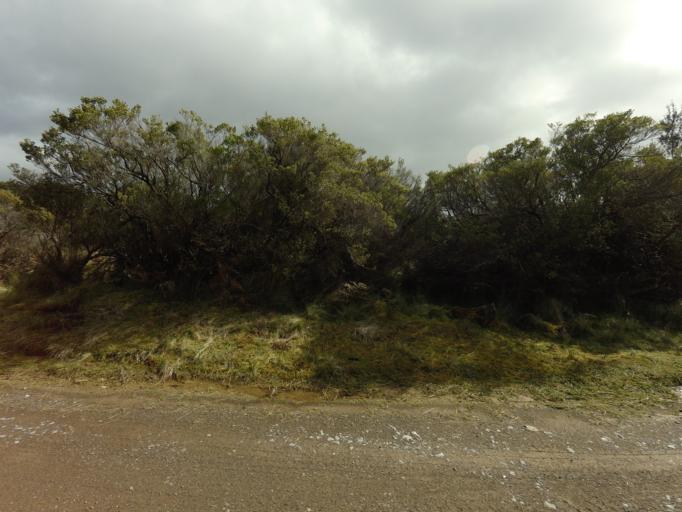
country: AU
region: Tasmania
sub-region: Huon Valley
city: Geeveston
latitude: -43.5825
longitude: 146.8964
